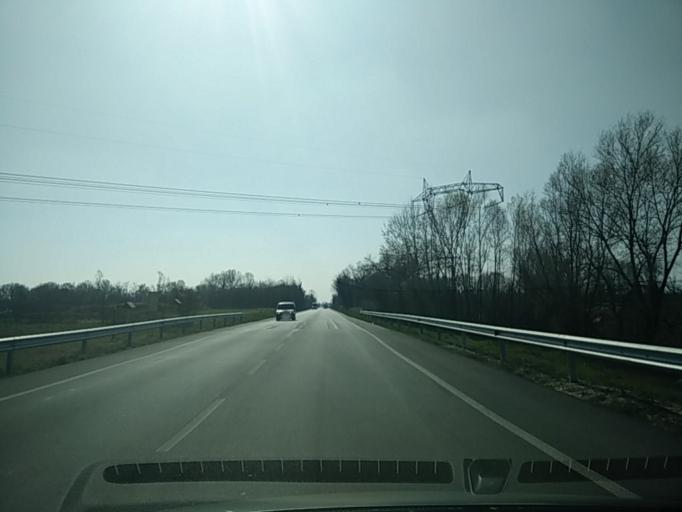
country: IT
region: Friuli Venezia Giulia
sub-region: Provincia di Pordenone
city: Azzano Decimo
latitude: 45.9170
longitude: 12.6309
